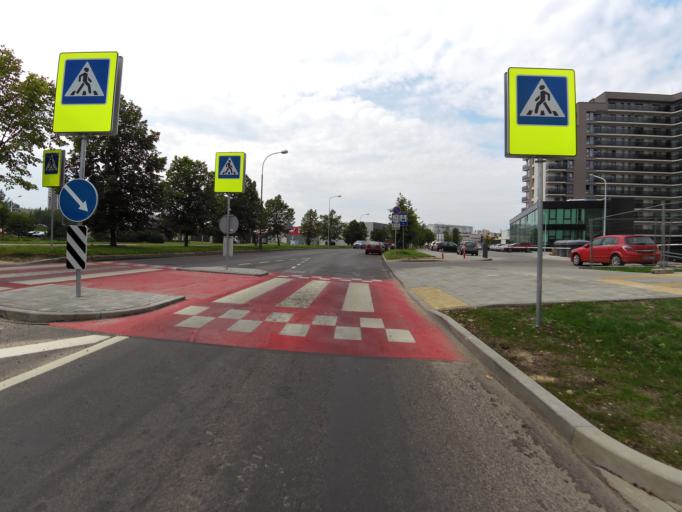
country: LT
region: Vilnius County
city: Seskine
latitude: 54.7203
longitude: 25.2485
